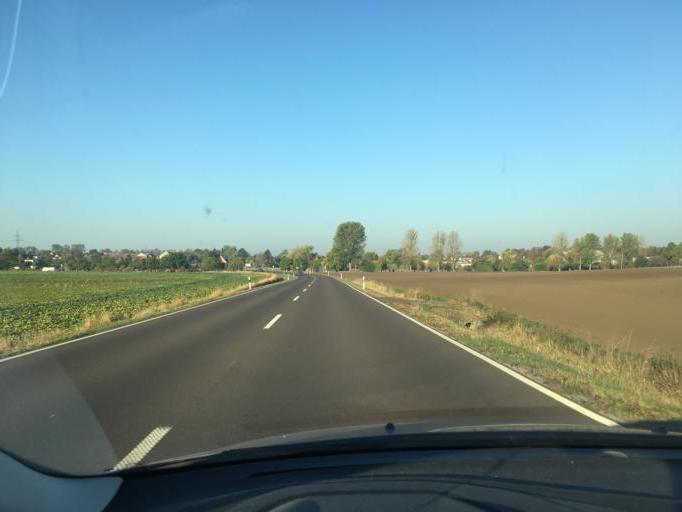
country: DE
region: Saxony-Anhalt
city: Welsleben
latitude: 52.0033
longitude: 11.6525
